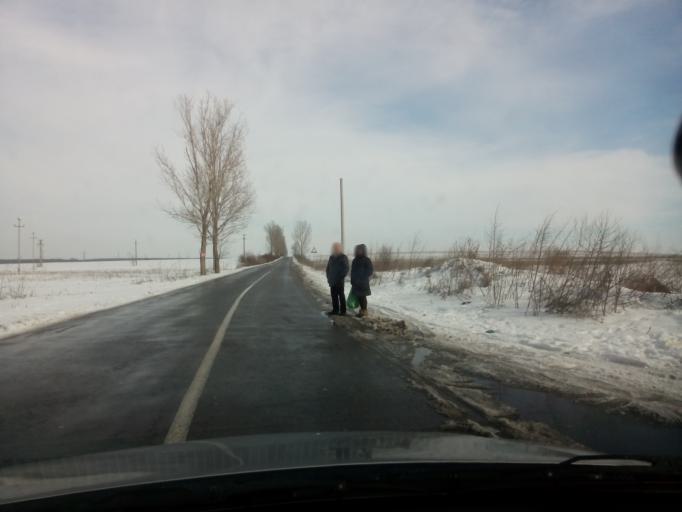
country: RO
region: Calarasi
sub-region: Comuna Soldanu
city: Soldanu
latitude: 44.2179
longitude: 26.5399
